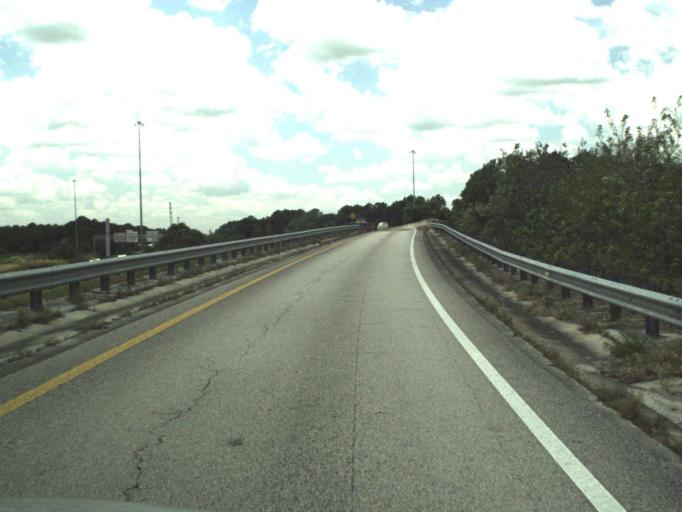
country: US
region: Florida
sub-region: Volusia County
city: South Daytona
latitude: 29.1549
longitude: -81.0774
